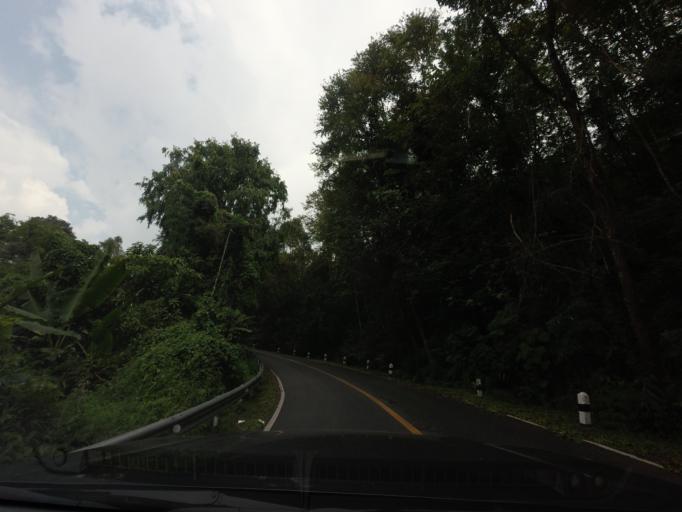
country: TH
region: Nan
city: Pua
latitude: 19.1888
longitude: 101.0185
